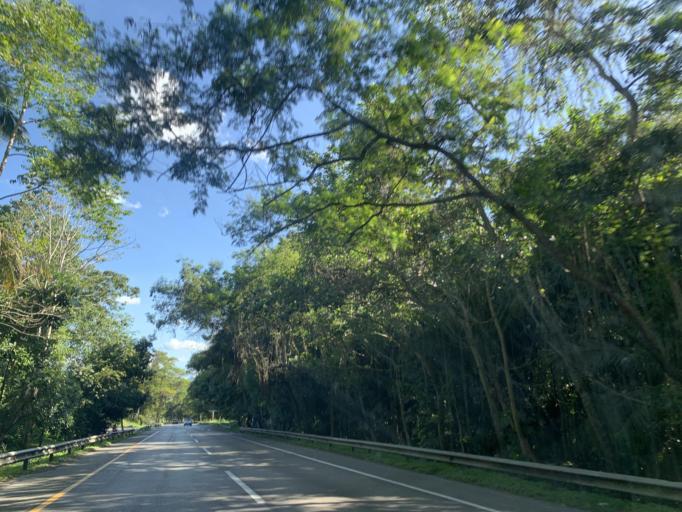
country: DO
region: San Cristobal
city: Villa Altagracia
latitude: 18.6491
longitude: -70.1676
